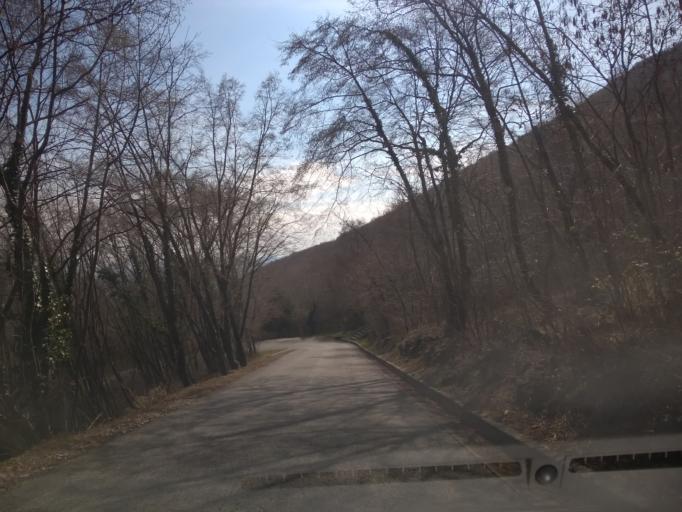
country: IT
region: Veneto
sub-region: Provincia di Vicenza
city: Piovene Rocchette
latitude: 45.7593
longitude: 11.4236
